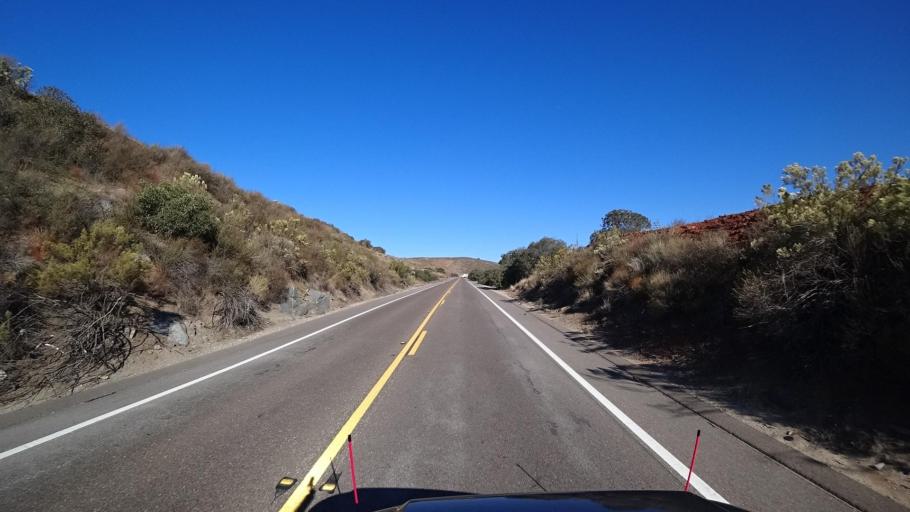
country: US
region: California
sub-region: San Diego County
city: Jamul
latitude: 32.6756
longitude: -116.8373
